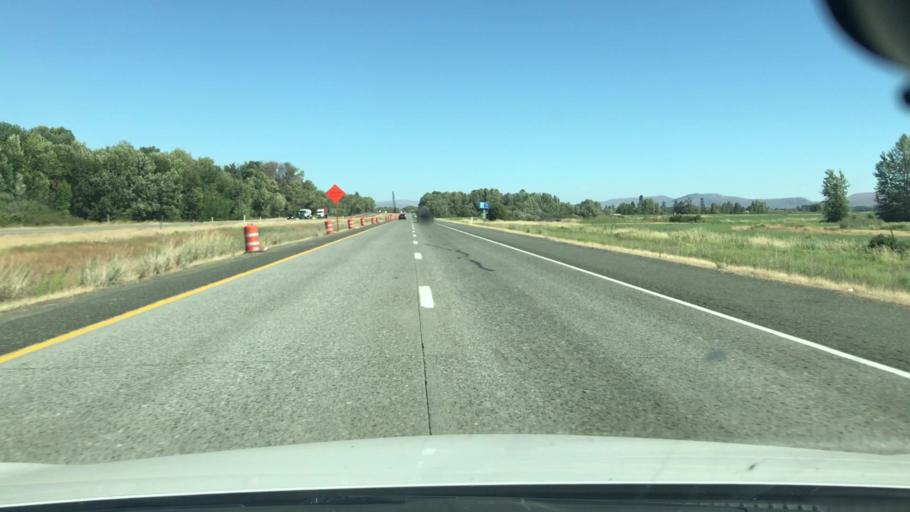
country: US
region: Washington
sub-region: Kittitas County
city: Ellensburg
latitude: 47.0484
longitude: -120.6503
